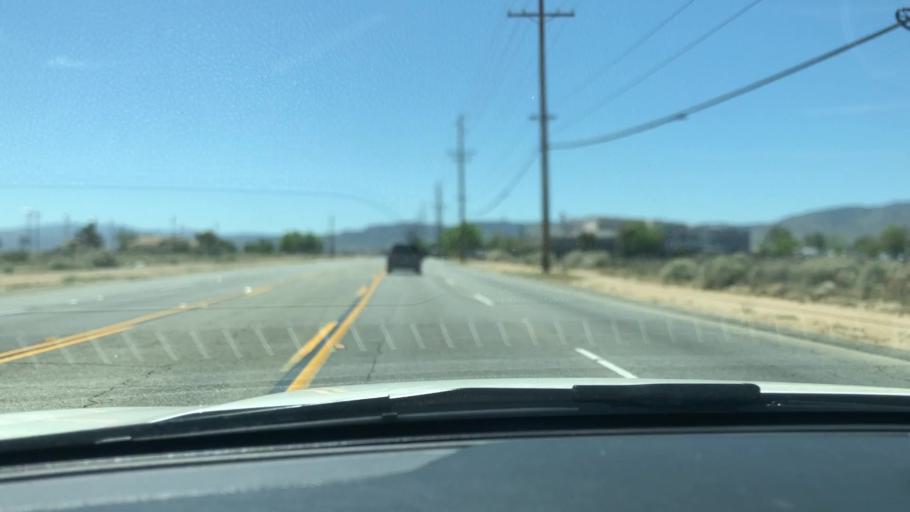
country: US
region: California
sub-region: Los Angeles County
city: Desert View Highlands
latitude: 34.6399
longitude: -118.1478
